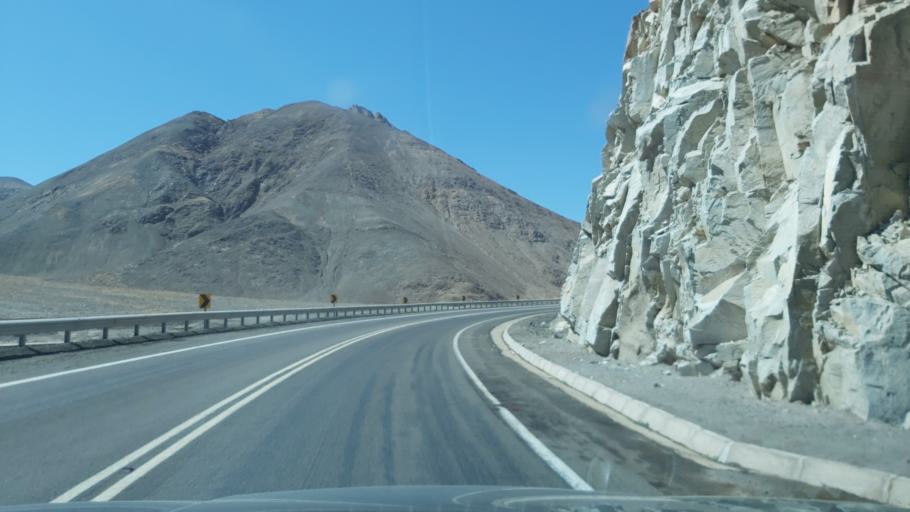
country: CL
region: Atacama
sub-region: Provincia de Chanaral
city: Diego de Almagro
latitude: -26.3380
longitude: -69.7470
